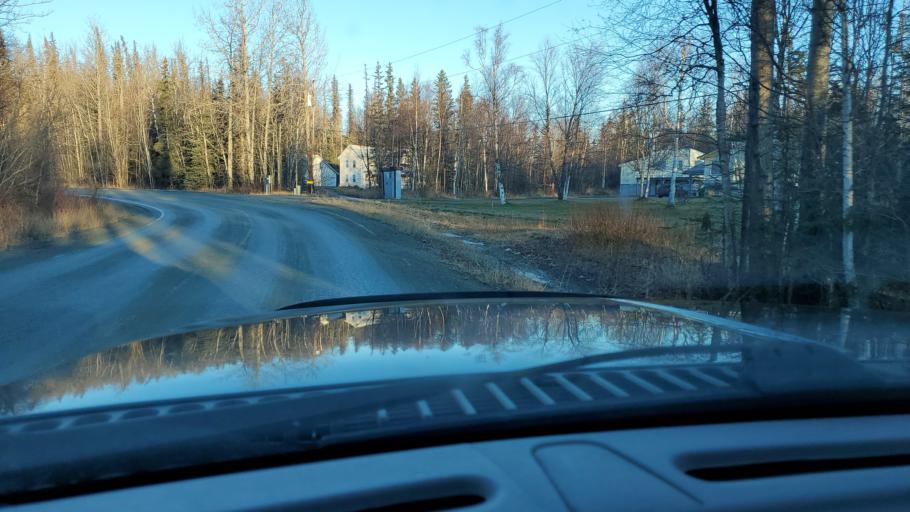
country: US
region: Alaska
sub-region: Matanuska-Susitna Borough
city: Gateway
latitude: 61.5899
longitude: -149.2451
